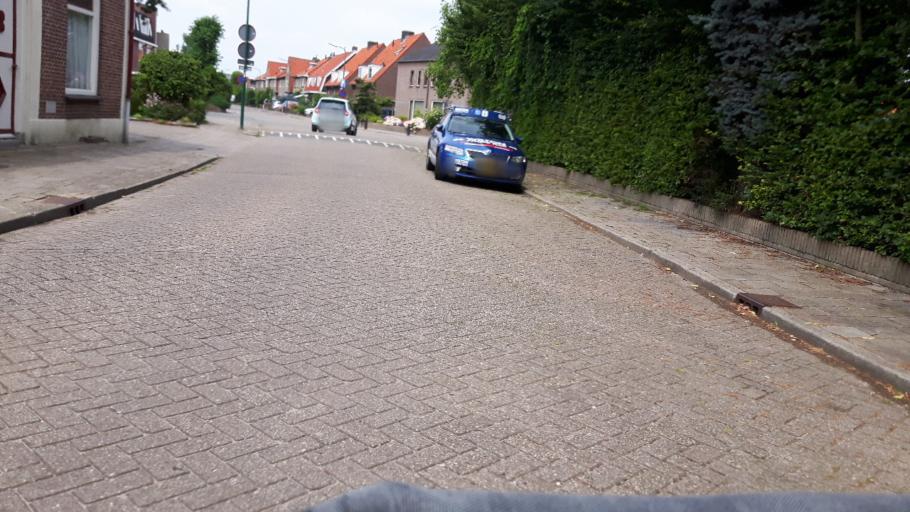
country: NL
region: Utrecht
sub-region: Gemeente Bunnik
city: Bunnik
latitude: 52.0649
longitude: 5.2020
